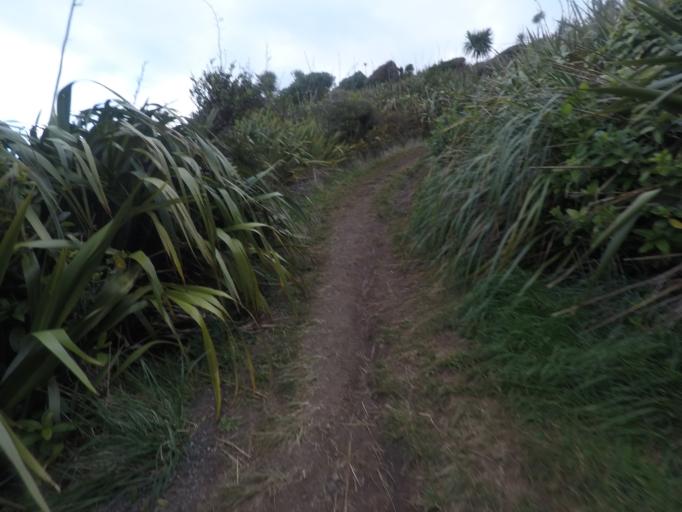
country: NZ
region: Auckland
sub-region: Auckland
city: Muriwai Beach
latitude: -36.9736
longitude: 174.4685
